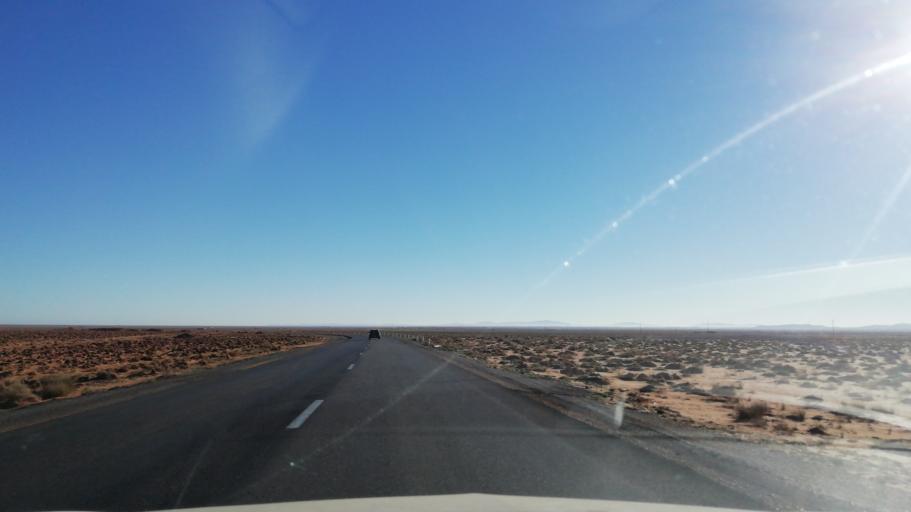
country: DZ
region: El Bayadh
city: El Bayadh
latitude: 33.8592
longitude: 0.5442
